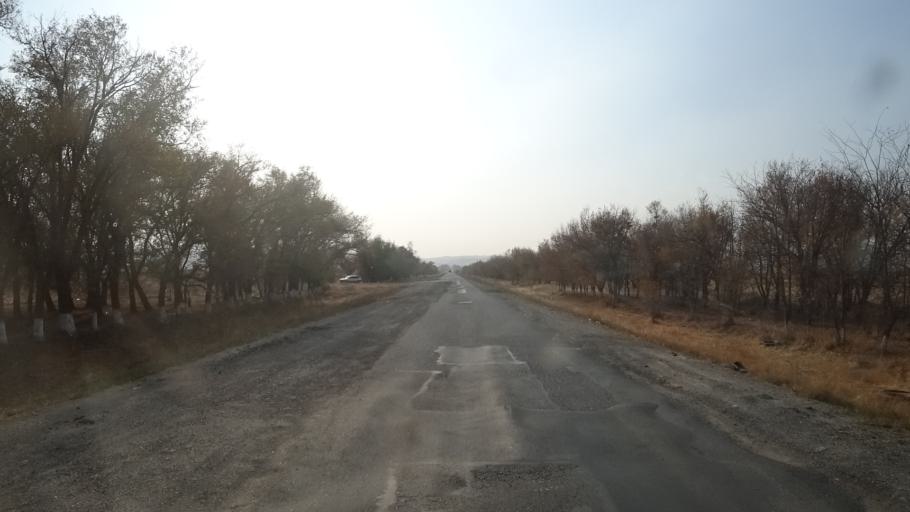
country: KZ
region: Zhambyl
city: Taraz
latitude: 42.7843
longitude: 71.0478
